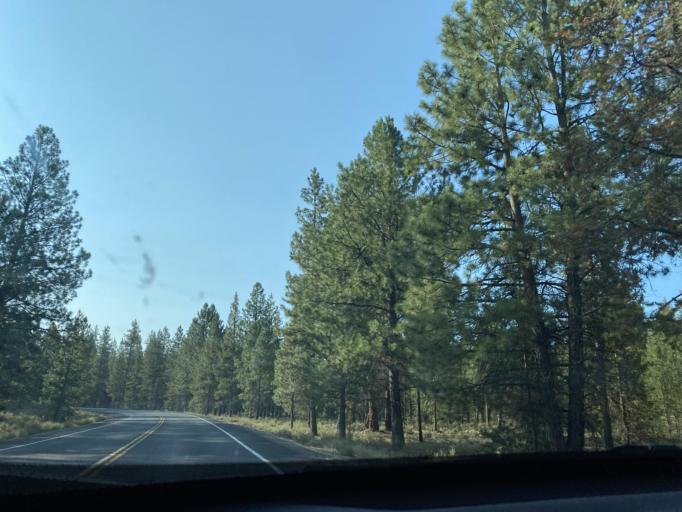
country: US
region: Oregon
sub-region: Deschutes County
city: La Pine
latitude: 43.7093
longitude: -121.4071
